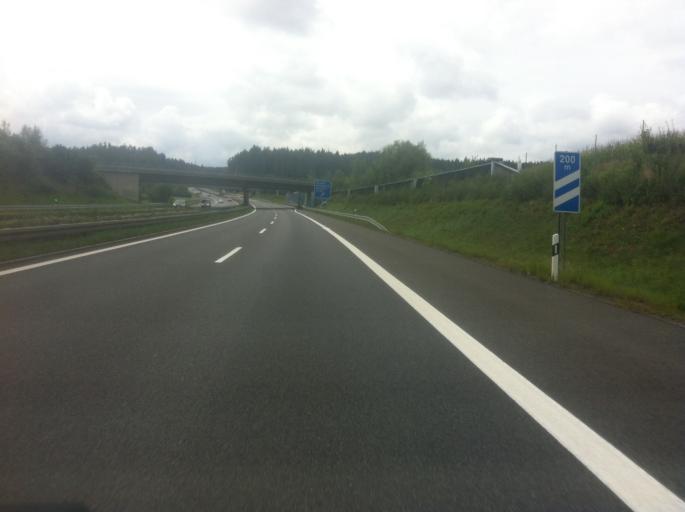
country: DE
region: Bavaria
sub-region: Upper Palatinate
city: Pleystein
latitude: 49.6215
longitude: 12.4201
